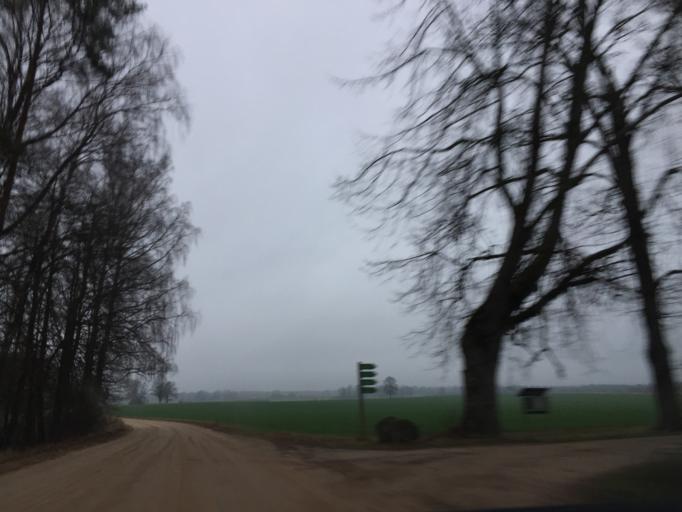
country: LV
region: Koceni
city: Koceni
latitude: 57.5400
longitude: 25.3321
